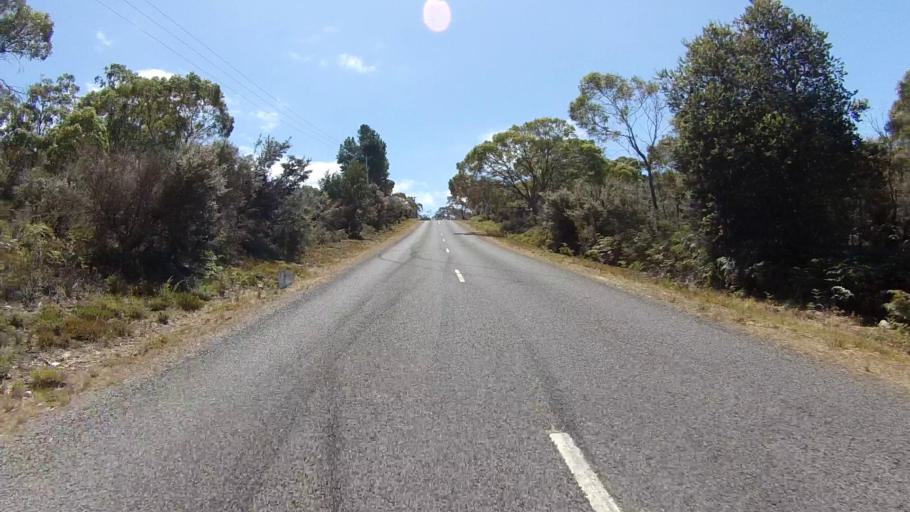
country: AU
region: Tasmania
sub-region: Clarence
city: Sandford
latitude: -43.0242
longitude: 147.4809
